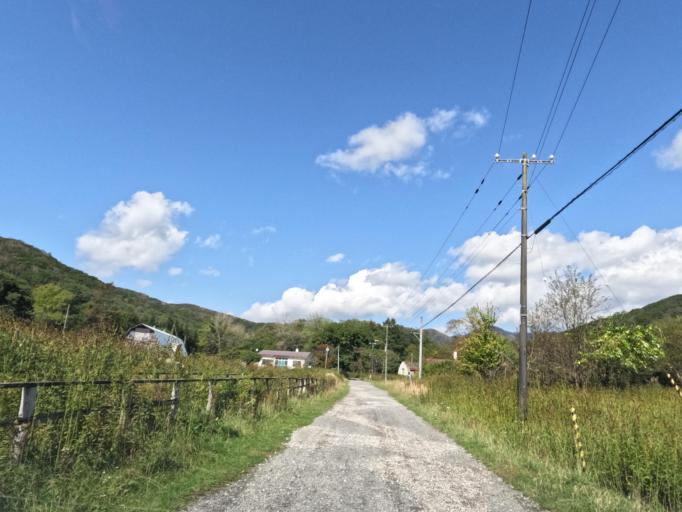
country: JP
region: Hokkaido
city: Muroran
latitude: 42.3902
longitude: 141.0314
